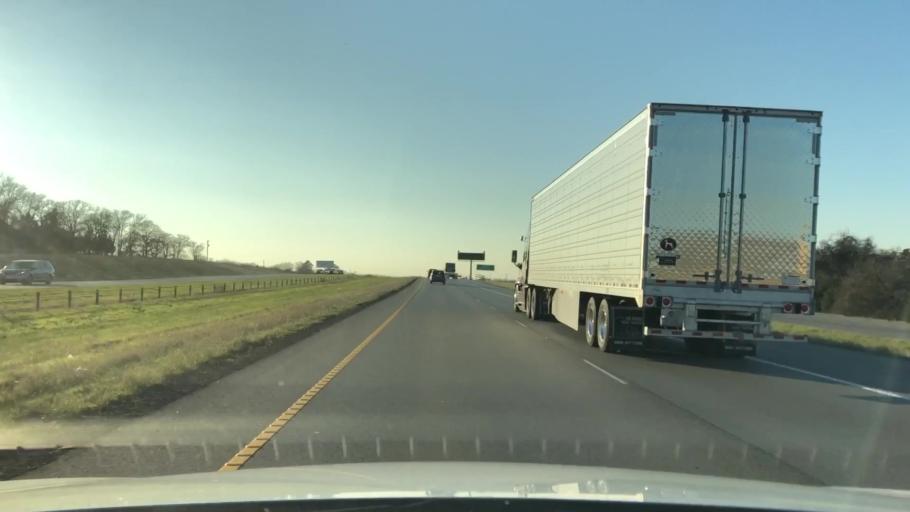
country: US
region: Texas
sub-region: Caldwell County
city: Luling
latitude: 29.6540
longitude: -97.5632
